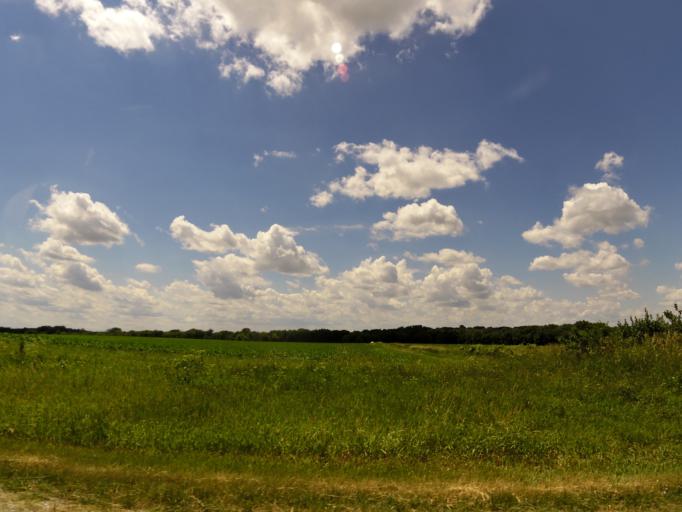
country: US
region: Iowa
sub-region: Buchanan County
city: Independence
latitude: 42.4903
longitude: -91.8895
